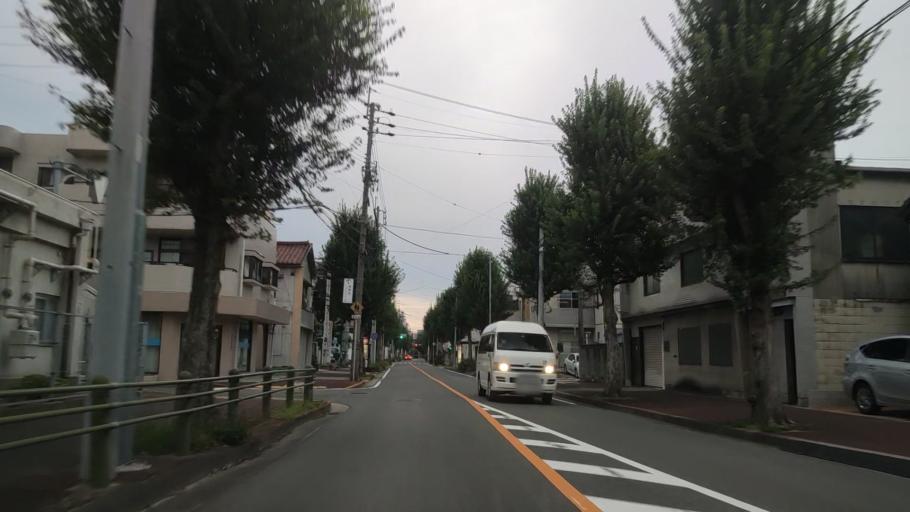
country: JP
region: Aichi
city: Nagoya-shi
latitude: 35.1883
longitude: 136.8958
